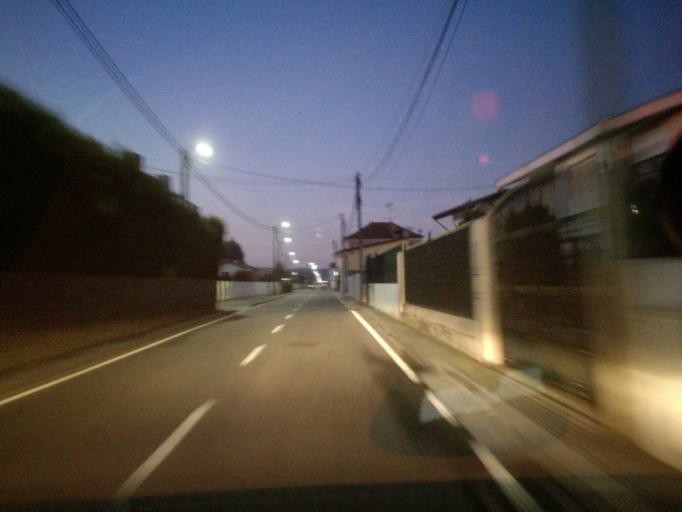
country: PT
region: Porto
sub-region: Maia
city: Nogueira
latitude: 41.2412
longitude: -8.5867
